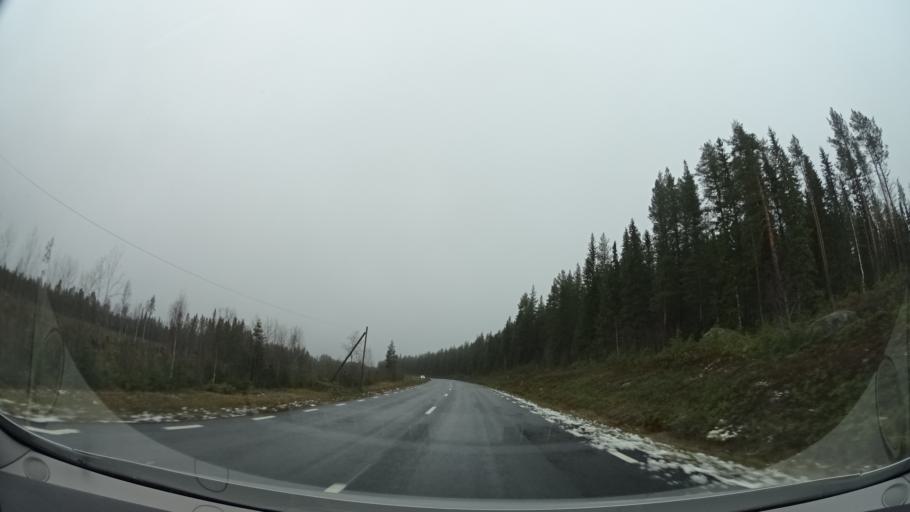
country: SE
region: Vaesterbotten
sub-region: Dorotea Kommun
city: Dorotea
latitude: 64.1925
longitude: 16.3012
